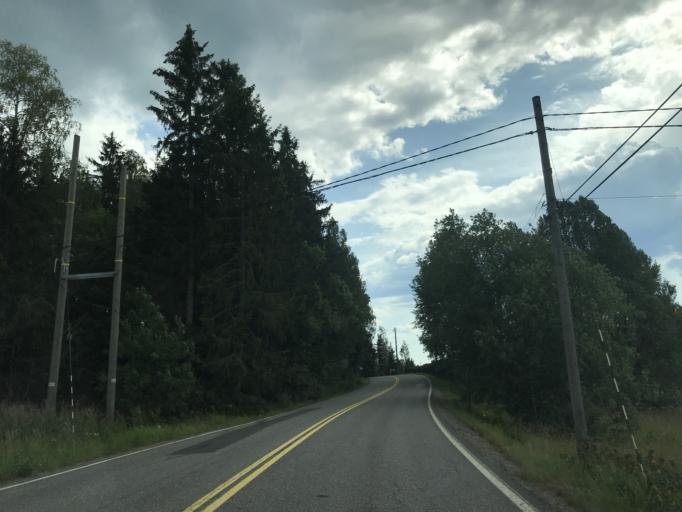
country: FI
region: Uusimaa
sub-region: Helsinki
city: Vihti
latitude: 60.3848
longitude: 24.3510
